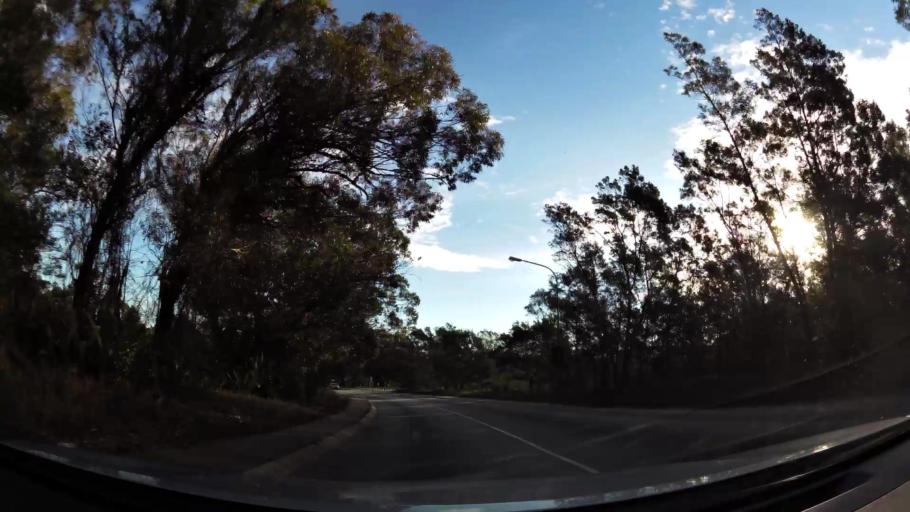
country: ZA
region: Eastern Cape
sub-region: Nelson Mandela Bay Metropolitan Municipality
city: Port Elizabeth
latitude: -33.9562
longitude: 25.5166
